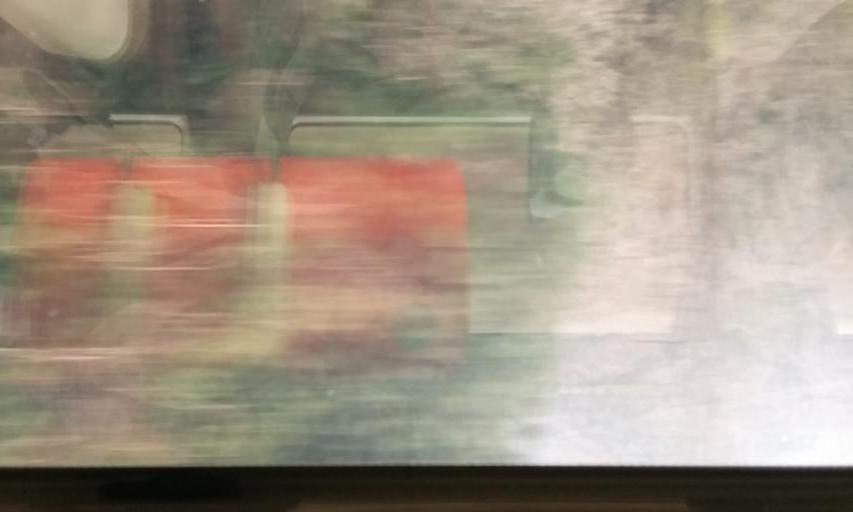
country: JP
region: Nagano
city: Shiojiri
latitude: 36.0615
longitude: 137.9001
